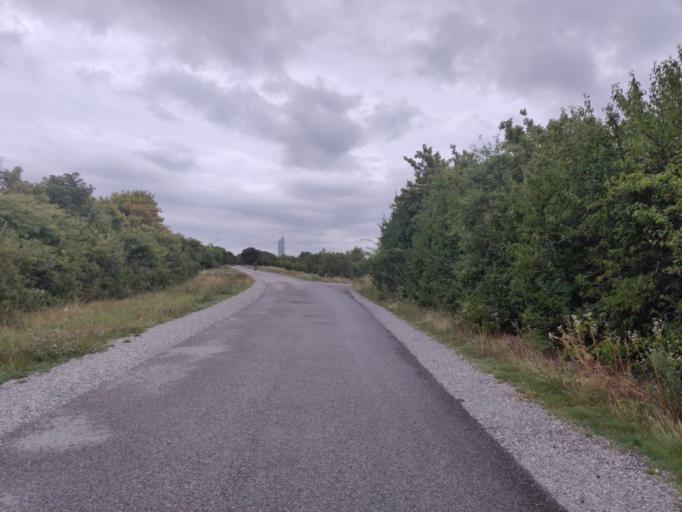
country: AT
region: Lower Austria
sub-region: Politischer Bezirk Korneuburg
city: Langenzersdorf
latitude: 48.2653
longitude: 16.3712
